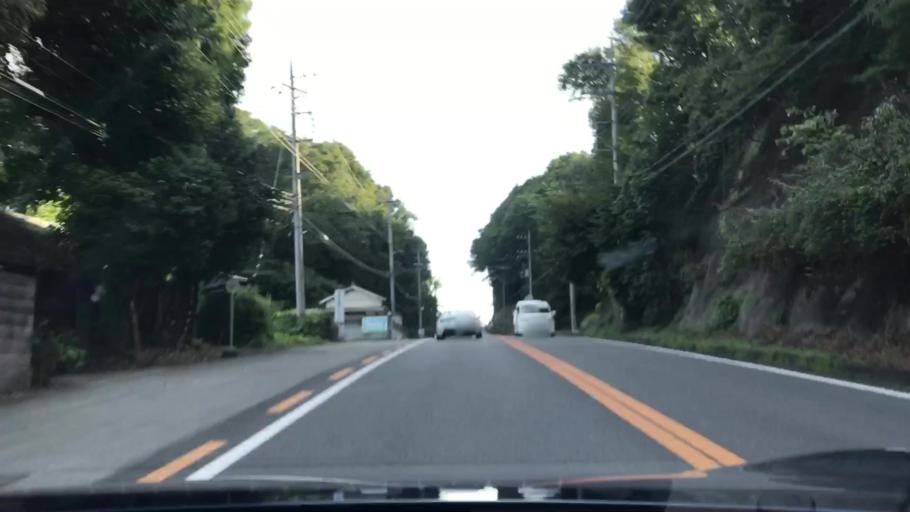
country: JP
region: Tochigi
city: Motegi
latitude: 36.5398
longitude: 140.2104
